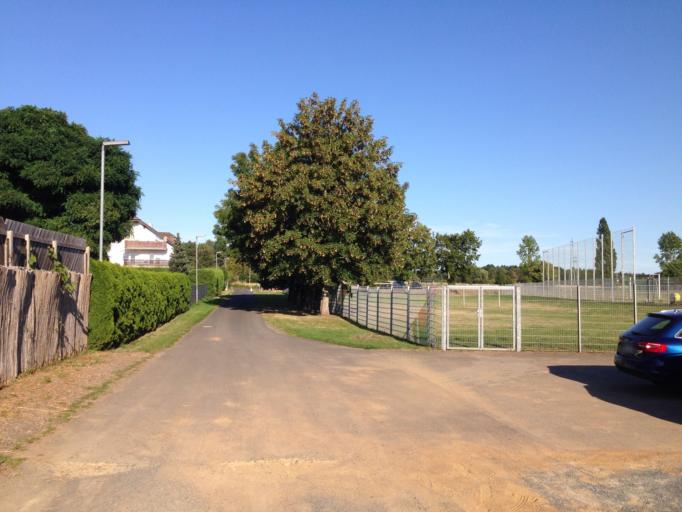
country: DE
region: Hesse
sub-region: Regierungsbezirk Giessen
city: Lich
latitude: 50.5316
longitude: 8.7531
